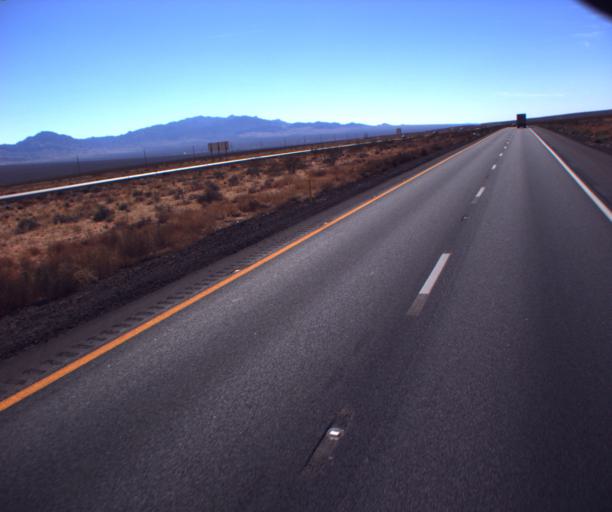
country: US
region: Arizona
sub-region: Mohave County
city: Beaver Dam
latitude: 36.8821
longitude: -113.9451
